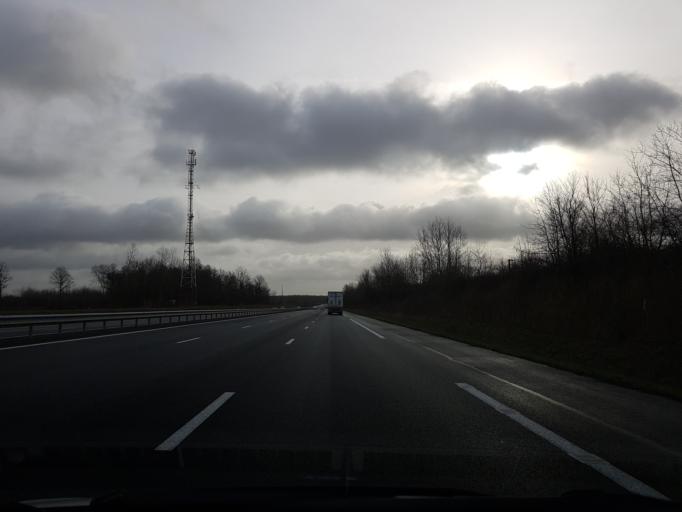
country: FR
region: Ile-de-France
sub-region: Departement de Seine-et-Marne
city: La Chapelle-Gauthier
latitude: 48.4732
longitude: 2.8713
